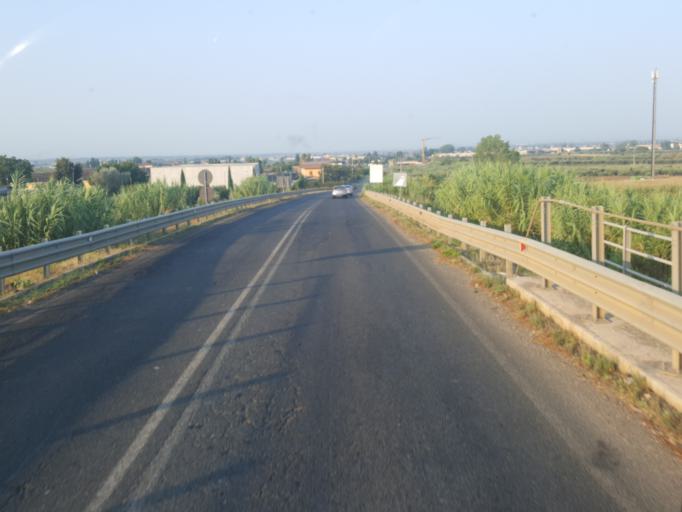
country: IT
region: Latium
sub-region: Provincia di Latina
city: Sezze Scalo
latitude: 41.4909
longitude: 13.0379
